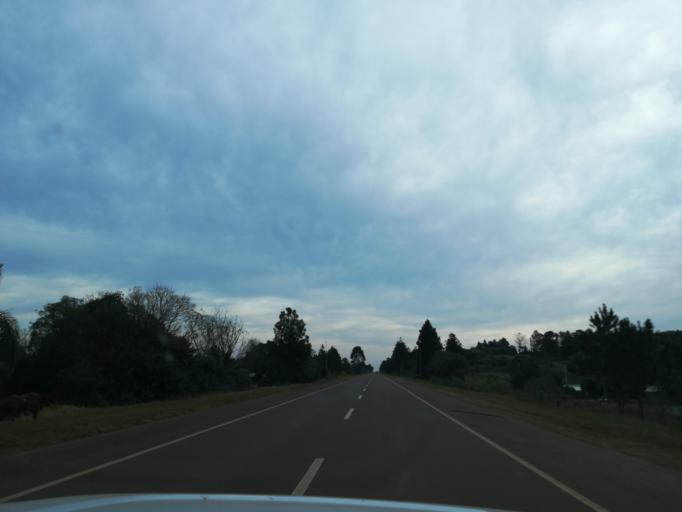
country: AR
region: Misiones
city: San Vicente
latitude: -26.7848
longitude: -54.3165
